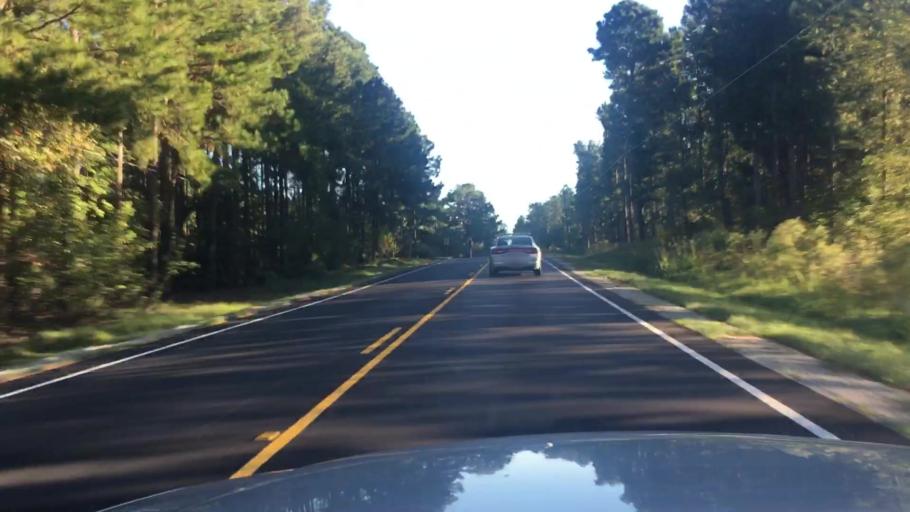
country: US
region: North Carolina
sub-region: Harnett County
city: Walkertown
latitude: 35.3324
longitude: -78.8620
